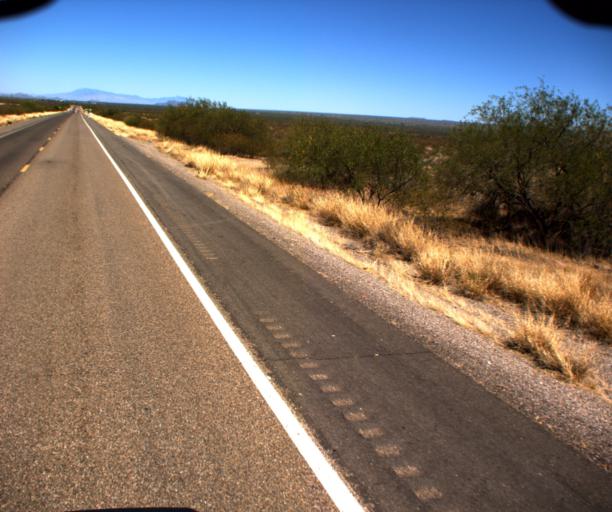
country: US
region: Arizona
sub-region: Pima County
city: Three Points
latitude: 32.0633
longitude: -111.3822
